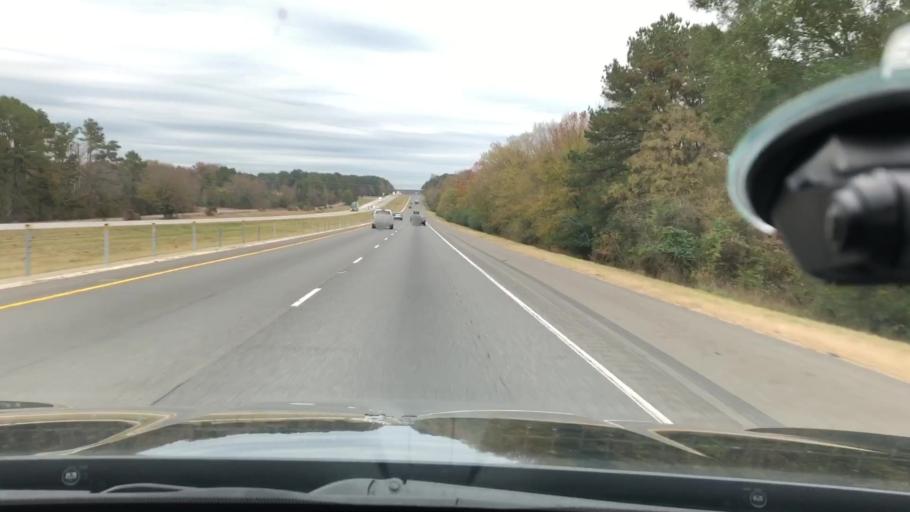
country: US
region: Arkansas
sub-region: Hot Spring County
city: Malvern
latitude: 34.3249
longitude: -92.9276
